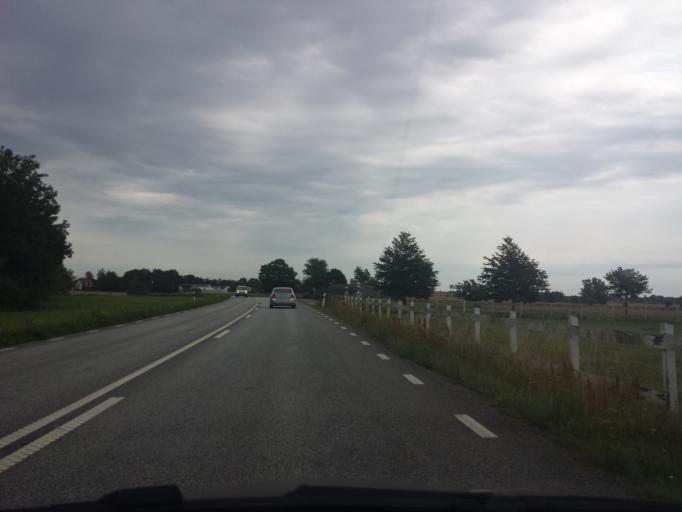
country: SE
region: Skane
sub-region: Ystads Kommun
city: Kopingebro
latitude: 55.4435
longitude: 14.0089
